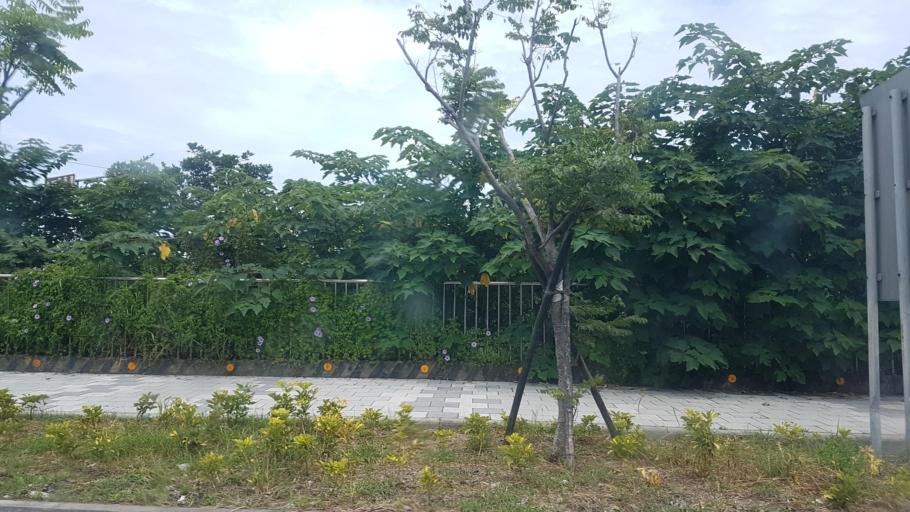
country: TW
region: Taiwan
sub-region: Hualien
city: Hualian
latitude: 24.0011
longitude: 121.6343
